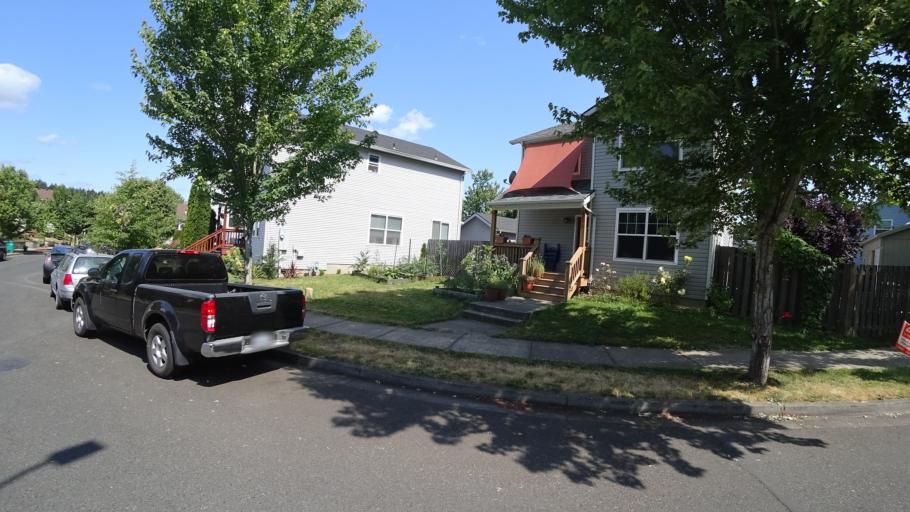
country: US
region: Oregon
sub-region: Washington County
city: West Haven
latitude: 45.6008
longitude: -122.7458
